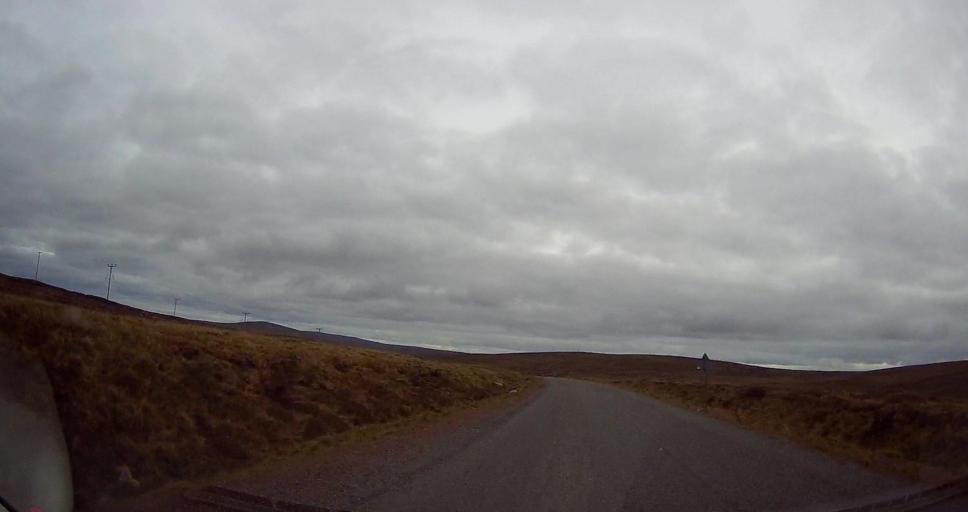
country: GB
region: Scotland
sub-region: Shetland Islands
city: Shetland
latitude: 60.6271
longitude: -1.0708
